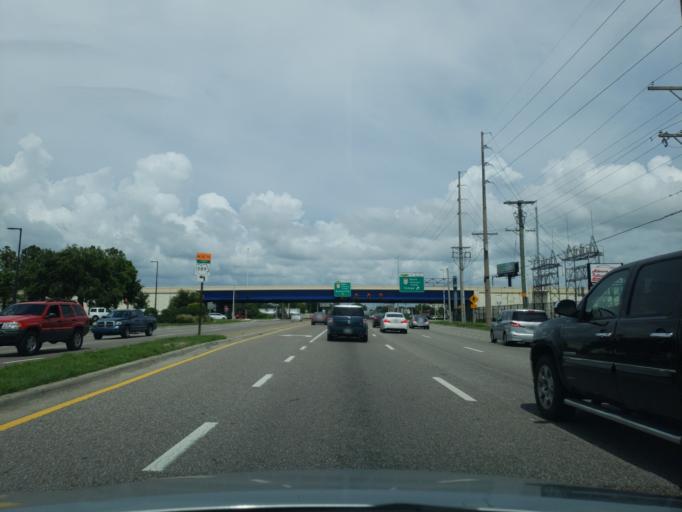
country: US
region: Florida
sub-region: Hillsborough County
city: Town 'n' Country
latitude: 28.0256
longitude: -82.5460
